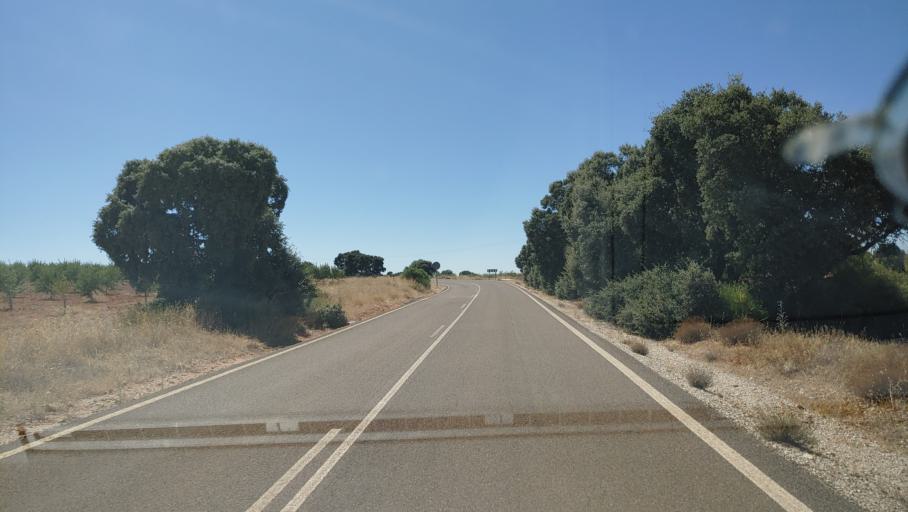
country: ES
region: Castille-La Mancha
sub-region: Provincia de Ciudad Real
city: Villahermosa
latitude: 38.8338
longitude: -2.8231
